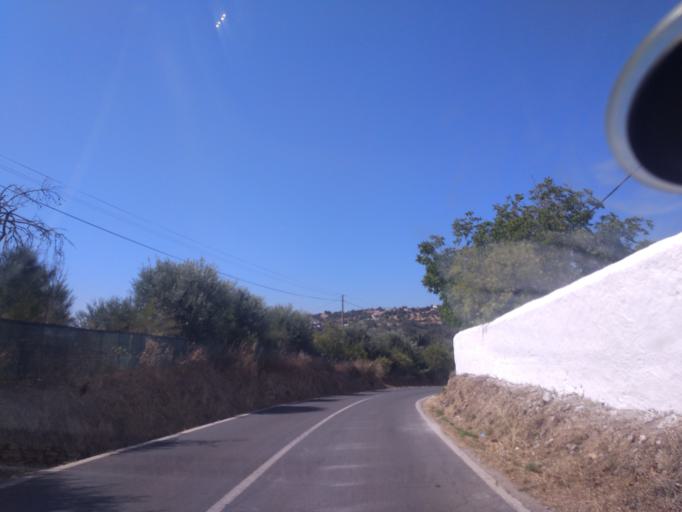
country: PT
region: Faro
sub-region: Sao Bras de Alportel
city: Sao Bras de Alportel
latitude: 37.1520
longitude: -7.9329
